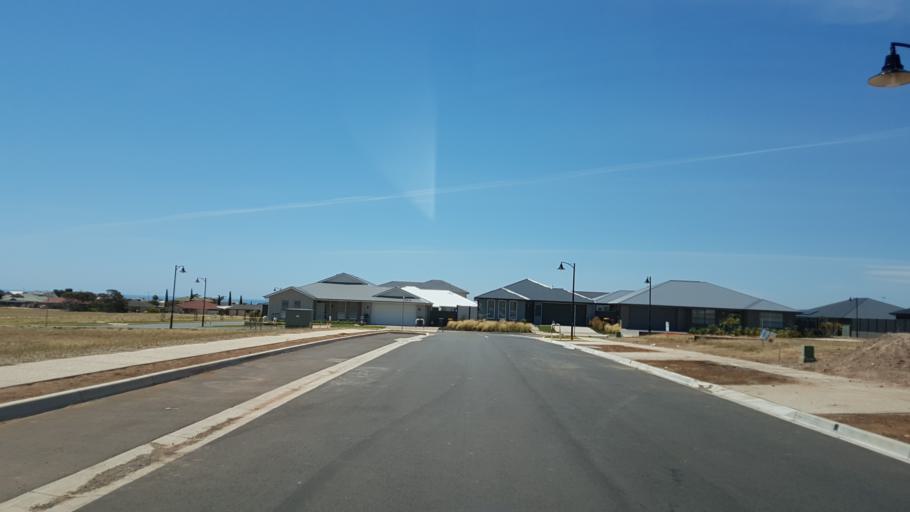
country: AU
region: South Australia
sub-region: Onkaparinga
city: Moana
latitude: -35.2183
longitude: 138.4756
